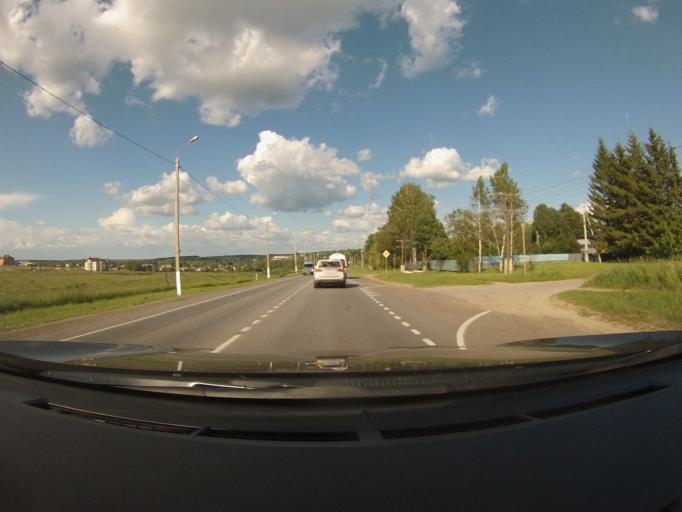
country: RU
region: Tula
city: Chern'
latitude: 53.4520
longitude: 36.8934
